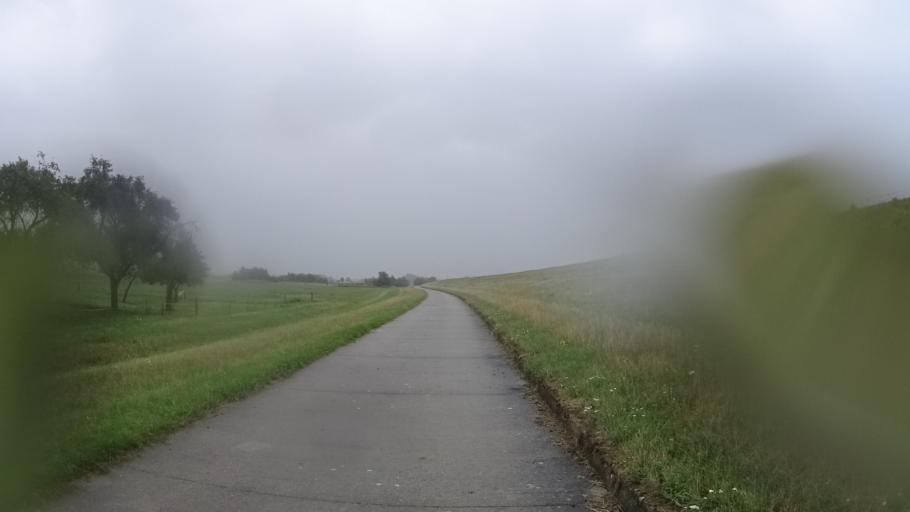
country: DE
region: Lower Saxony
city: Hitzacker
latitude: 53.1809
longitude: 11.0196
